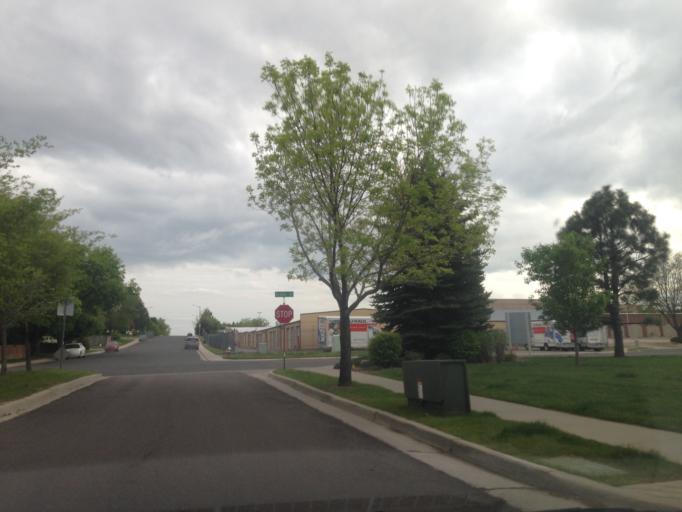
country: US
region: Colorado
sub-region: Boulder County
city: Longmont
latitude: 40.1419
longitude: -105.0997
